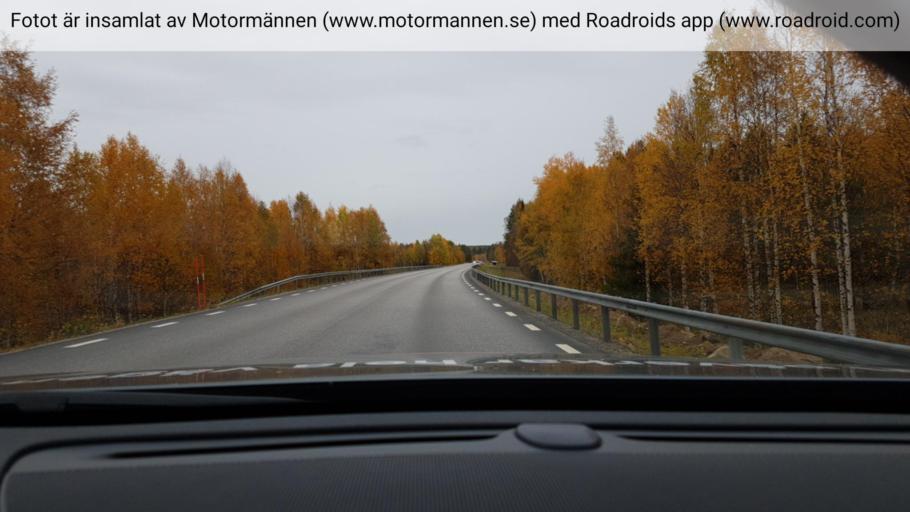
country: SE
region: Norrbotten
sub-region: Overkalix Kommun
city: OEverkalix
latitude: 66.3541
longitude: 22.8273
